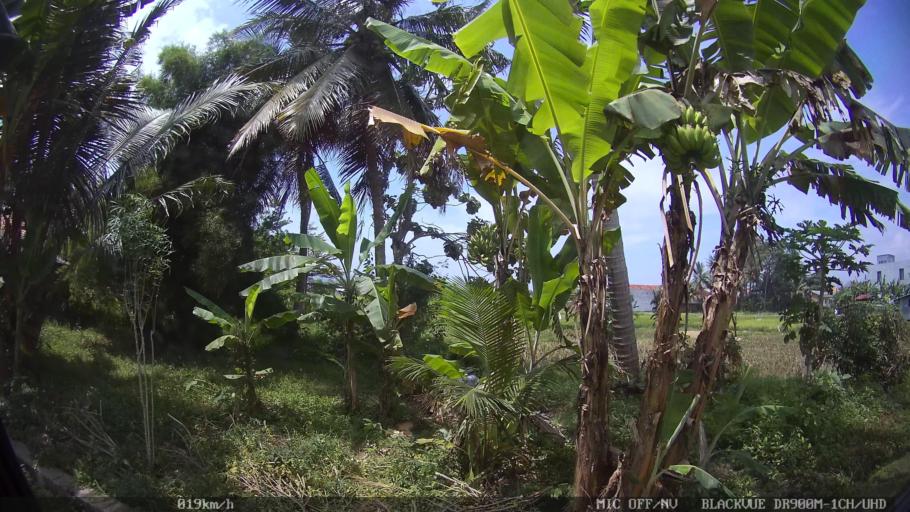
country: ID
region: Lampung
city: Kedaton
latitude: -5.3736
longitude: 105.3057
